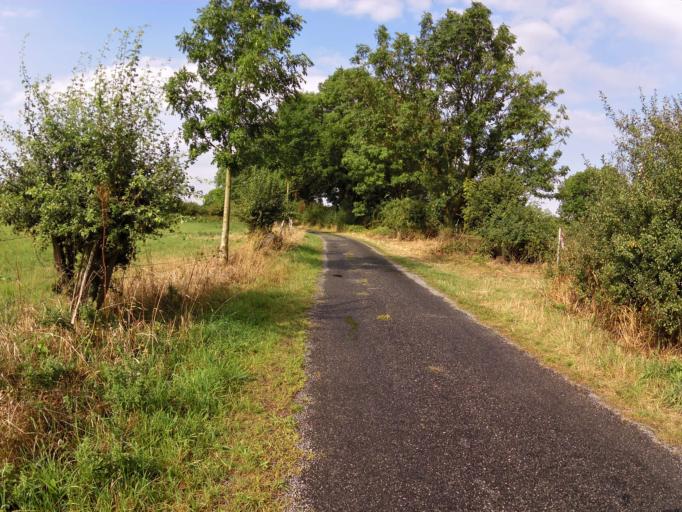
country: DE
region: Lower Saxony
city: Marklohe
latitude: 52.6608
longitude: 9.1815
